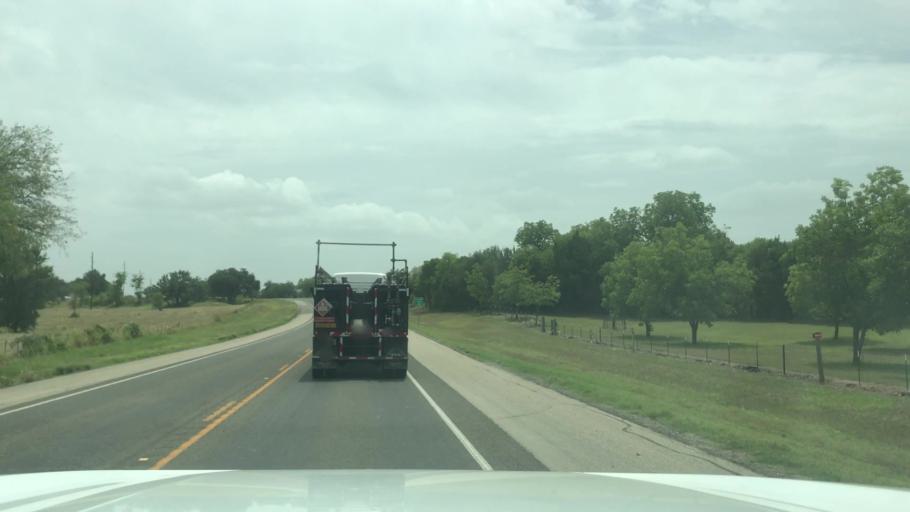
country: US
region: Texas
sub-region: Bosque County
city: Clifton
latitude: 31.7089
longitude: -97.5456
